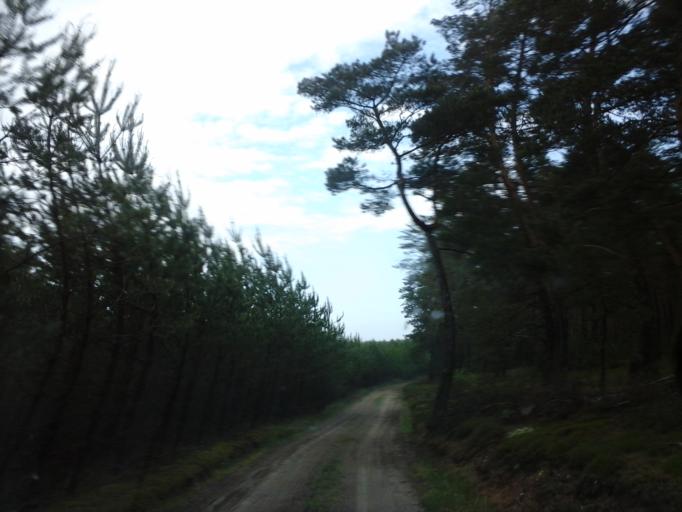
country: PL
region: West Pomeranian Voivodeship
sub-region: Powiat choszczenski
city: Drawno
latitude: 53.2639
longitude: 15.7774
